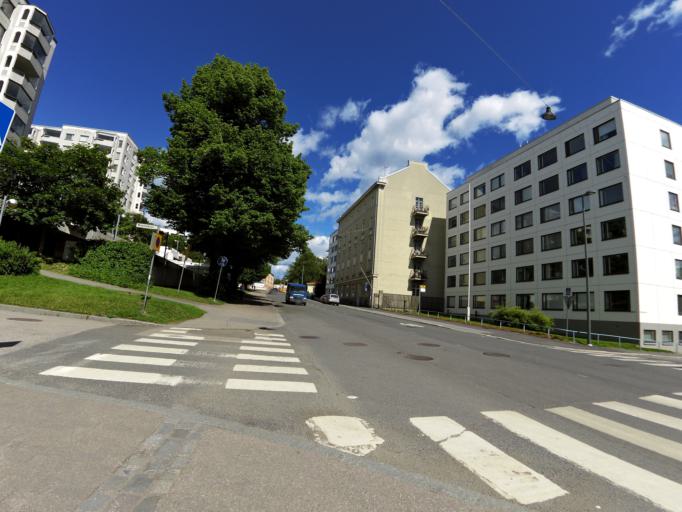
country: FI
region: Pirkanmaa
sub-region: Tampere
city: Tampere
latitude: 61.5036
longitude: 23.7671
